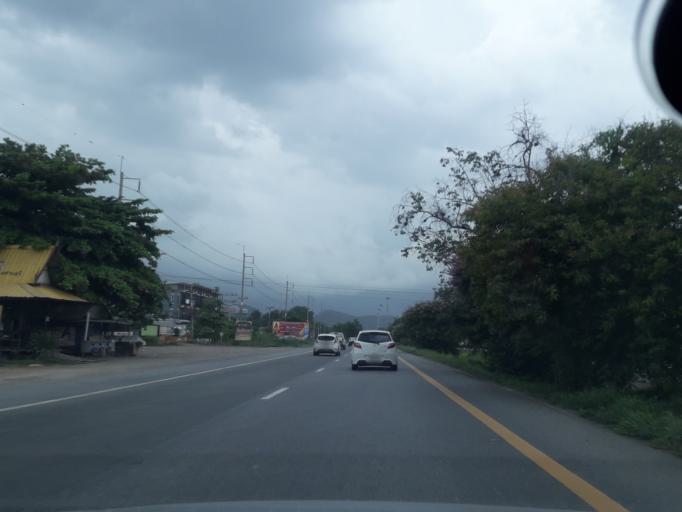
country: TH
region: Sara Buri
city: Saraburi
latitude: 14.5090
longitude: 100.9063
